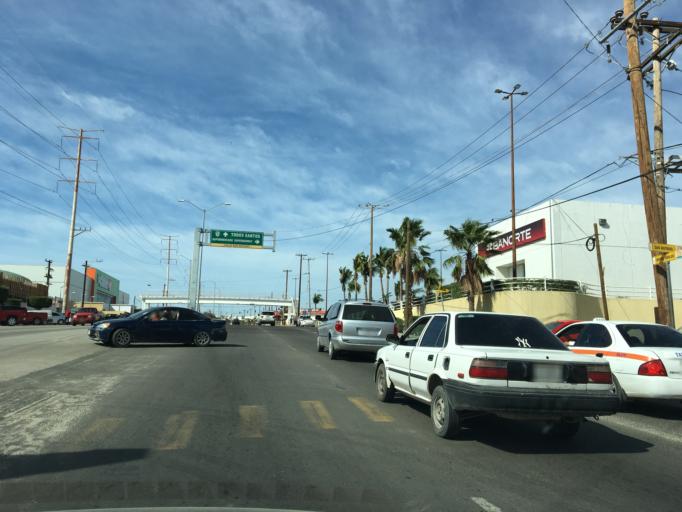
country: MX
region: Baja California Sur
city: Cabo San Lucas
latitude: 22.8999
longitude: -109.9276
